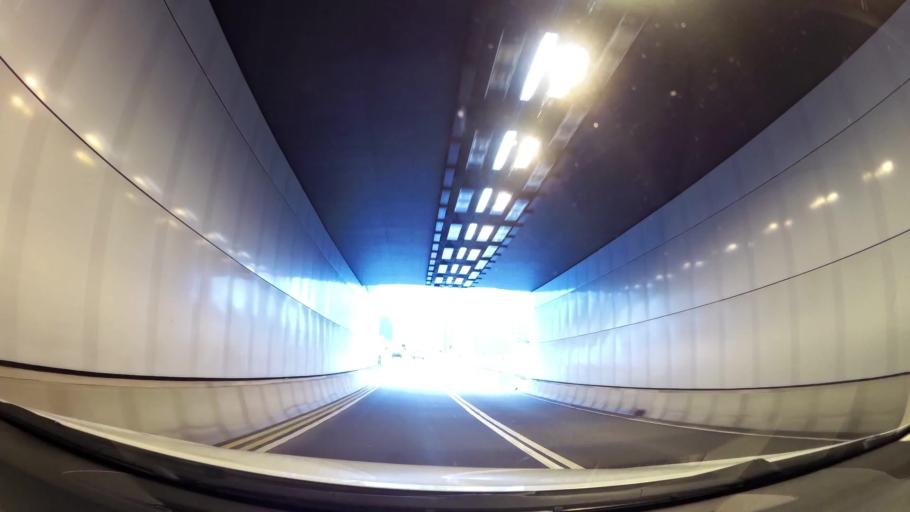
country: HK
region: Wanchai
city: Wan Chai
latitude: 22.2823
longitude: 114.1659
